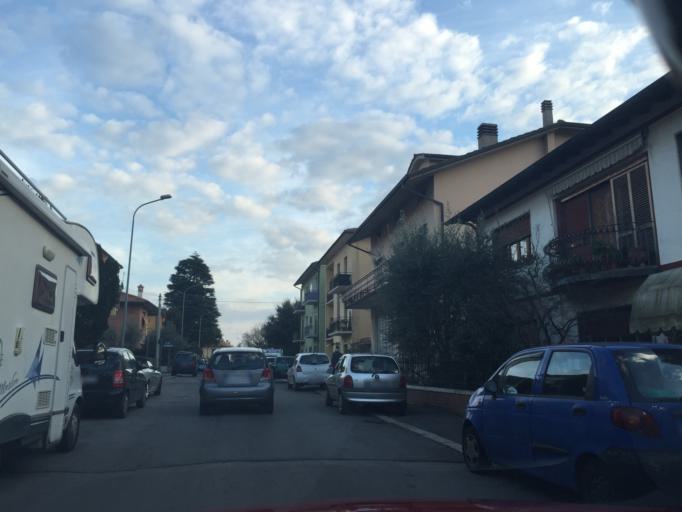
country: IT
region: Tuscany
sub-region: Provincia di Pistoia
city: Monsummano Terme
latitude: 43.8697
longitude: 10.8158
